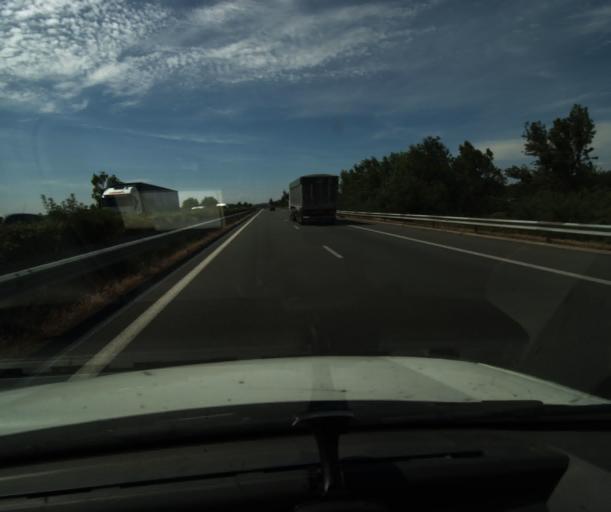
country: FR
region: Midi-Pyrenees
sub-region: Departement du Tarn-et-Garonne
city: Saint-Porquier
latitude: 44.0403
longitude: 1.1512
